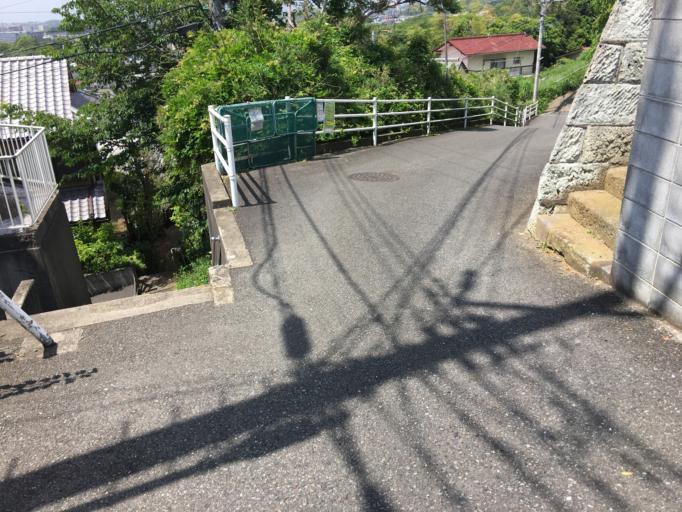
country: JP
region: Kanagawa
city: Kamakura
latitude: 35.3435
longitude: 139.5450
